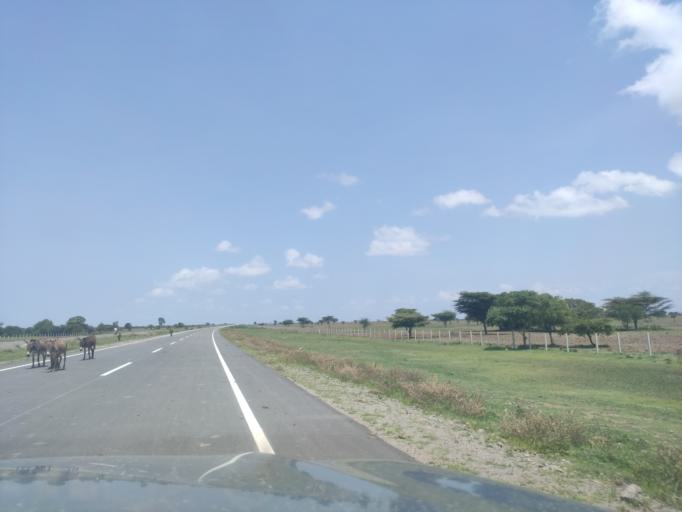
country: ET
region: Oromiya
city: Ziway
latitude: 8.2317
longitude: 38.8736
